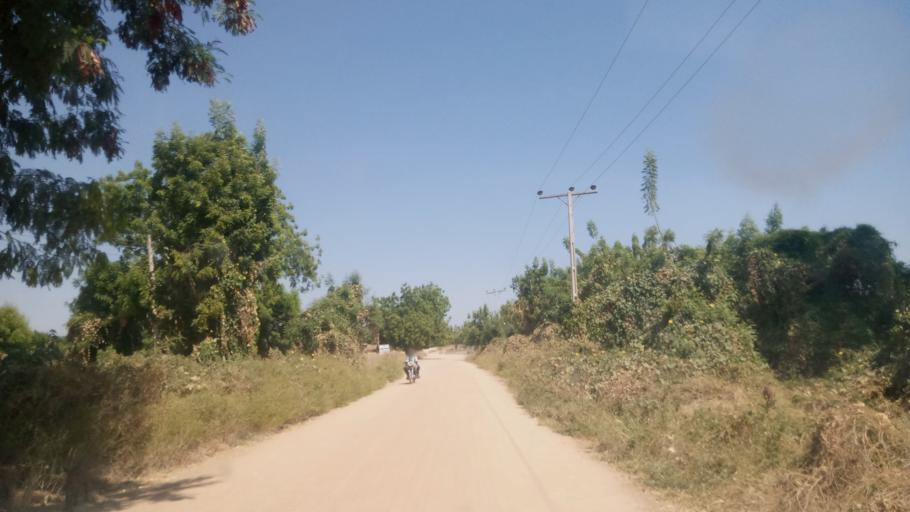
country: NG
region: Borno
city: Shani
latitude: 9.9009
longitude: 12.0078
